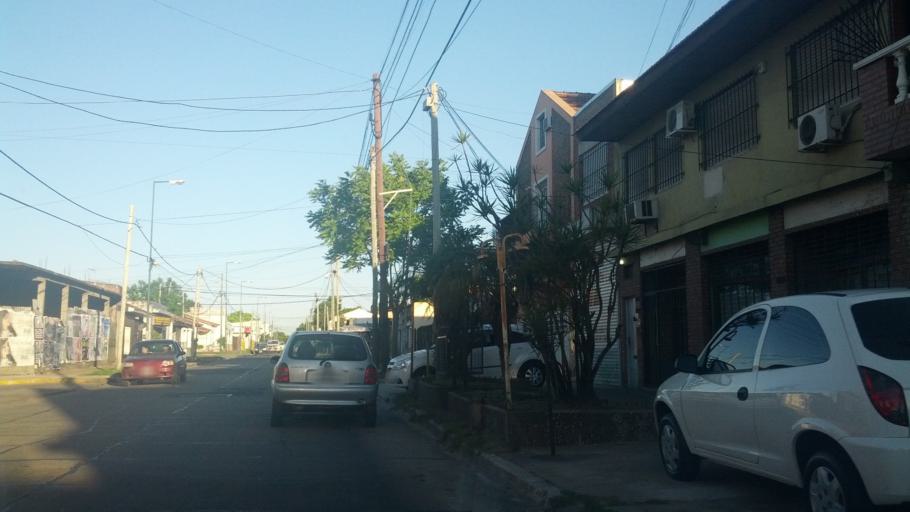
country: AR
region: Buenos Aires
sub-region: Partido de Lomas de Zamora
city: Lomas de Zamora
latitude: -34.7672
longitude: -58.4156
